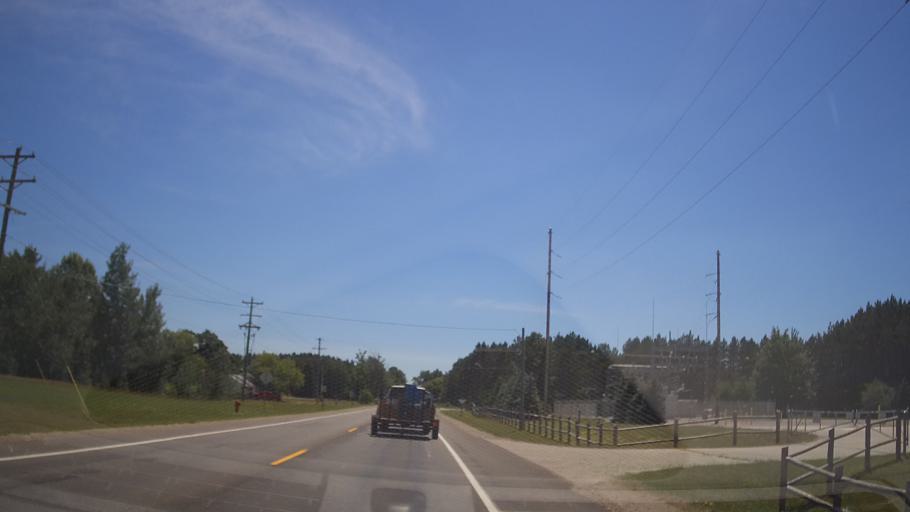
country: US
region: Michigan
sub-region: Grand Traverse County
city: Traverse City
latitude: 44.6555
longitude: -85.6965
